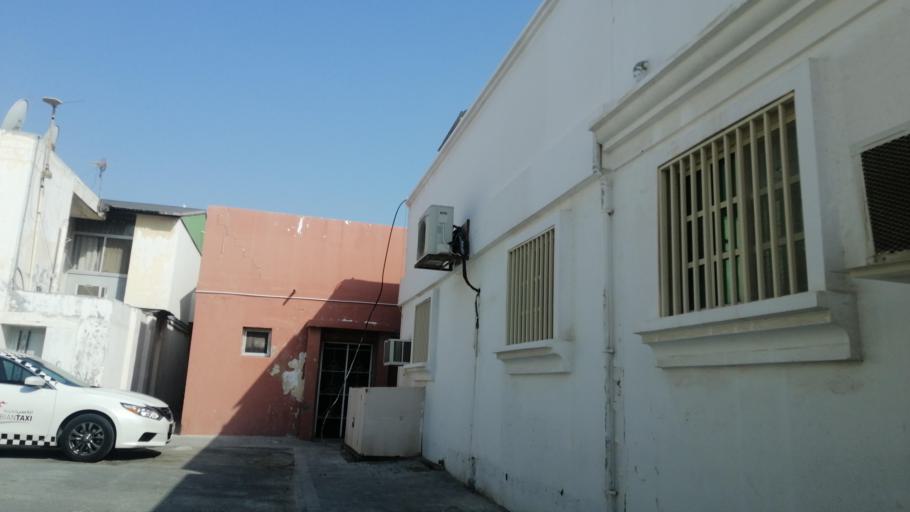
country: BH
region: Muharraq
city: Al Muharraq
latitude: 26.2577
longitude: 50.6345
